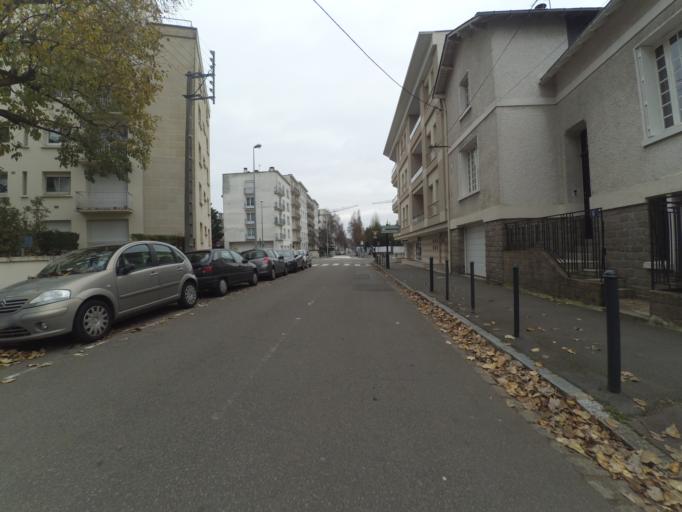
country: FR
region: Pays de la Loire
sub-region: Departement de la Loire-Atlantique
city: Nantes
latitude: 47.2261
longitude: -1.5712
